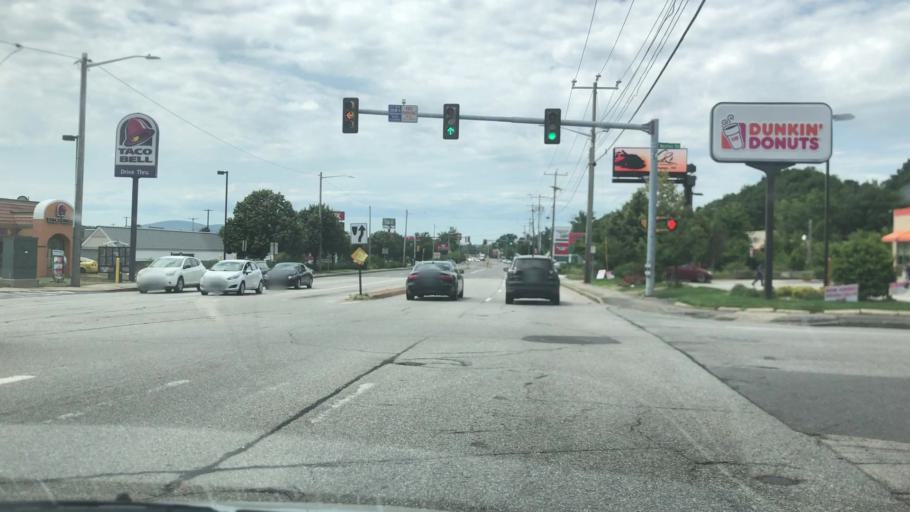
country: US
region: New Hampshire
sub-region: Hillsborough County
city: Manchester
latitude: 42.9619
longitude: -71.4397
